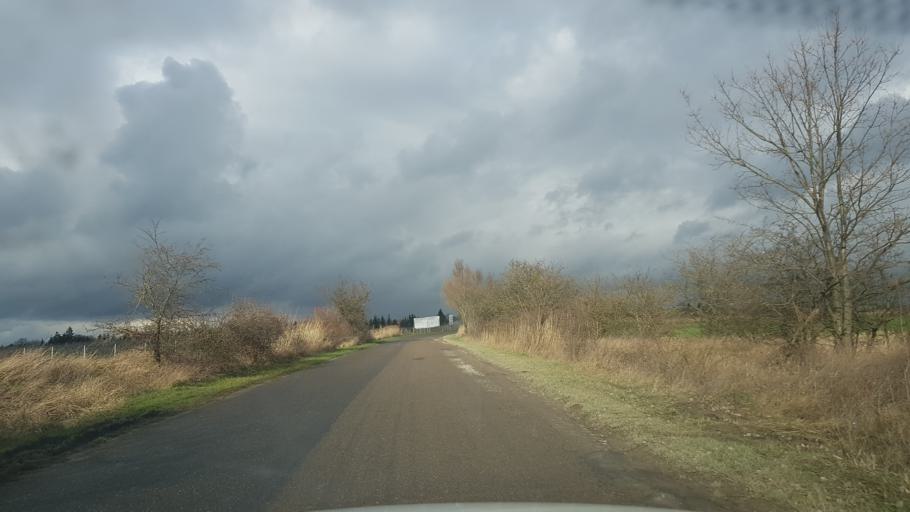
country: PL
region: West Pomeranian Voivodeship
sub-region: Powiat policki
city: Kolbaskowo
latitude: 53.3507
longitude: 14.4408
